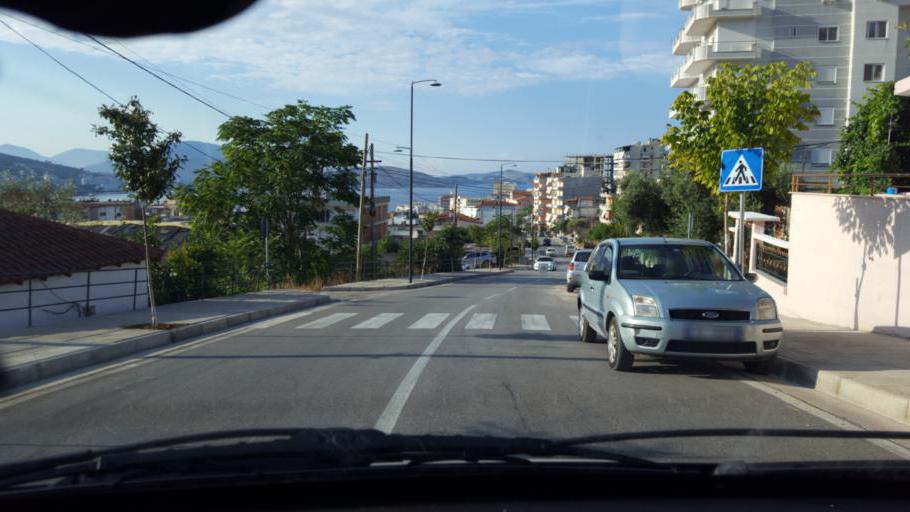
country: AL
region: Vlore
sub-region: Rrethi i Sarandes
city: Sarande
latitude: 39.8788
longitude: 20.0005
